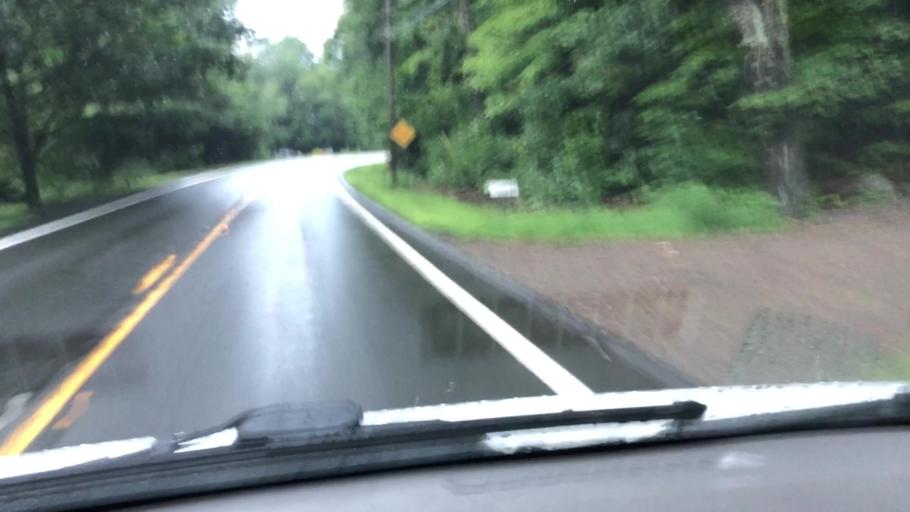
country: US
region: Massachusetts
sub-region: Hampshire County
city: Westhampton
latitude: 42.2785
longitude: -72.8655
